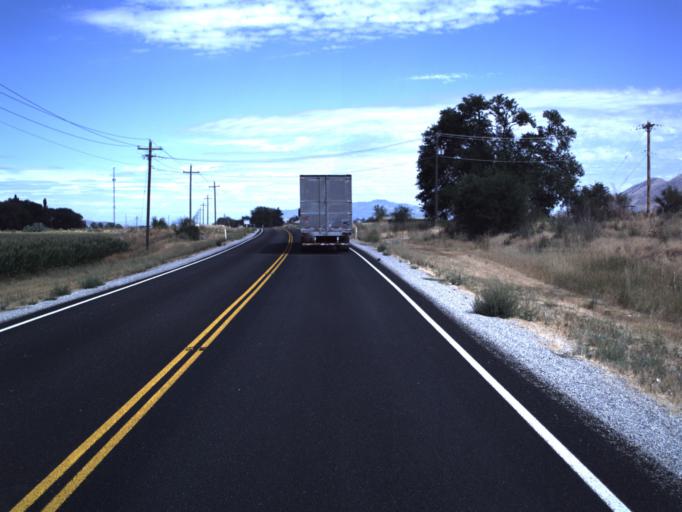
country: US
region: Utah
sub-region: Box Elder County
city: Honeyville
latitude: 41.6267
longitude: -112.1268
